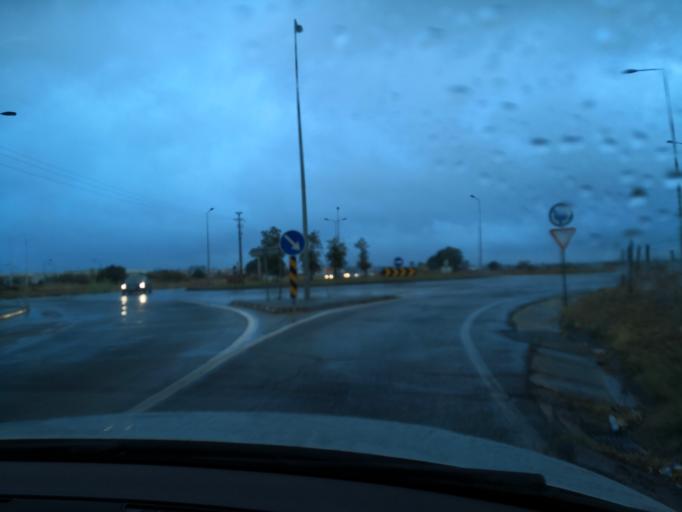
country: PT
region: Setubal
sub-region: Moita
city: Alhos Vedros
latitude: 38.6523
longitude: -9.0133
